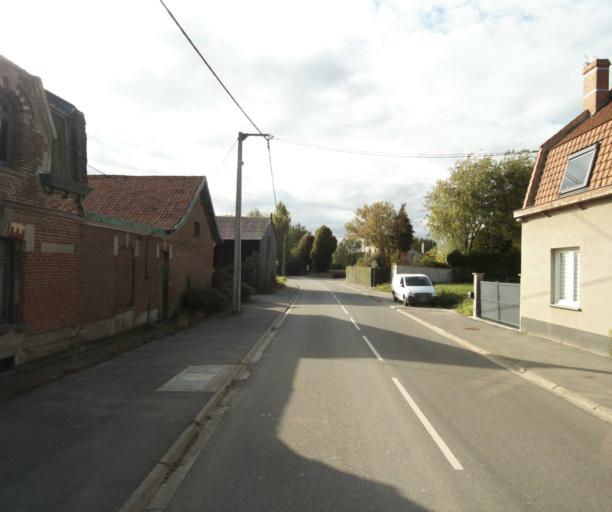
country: FR
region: Nord-Pas-de-Calais
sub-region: Departement du Nord
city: Ennetieres-en-Weppes
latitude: 50.6354
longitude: 2.9343
